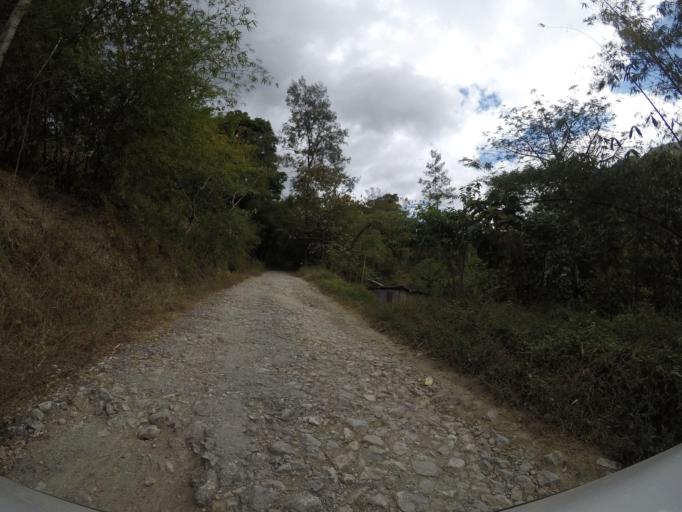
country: TL
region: Baucau
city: Baucau
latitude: -8.6238
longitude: 126.6568
